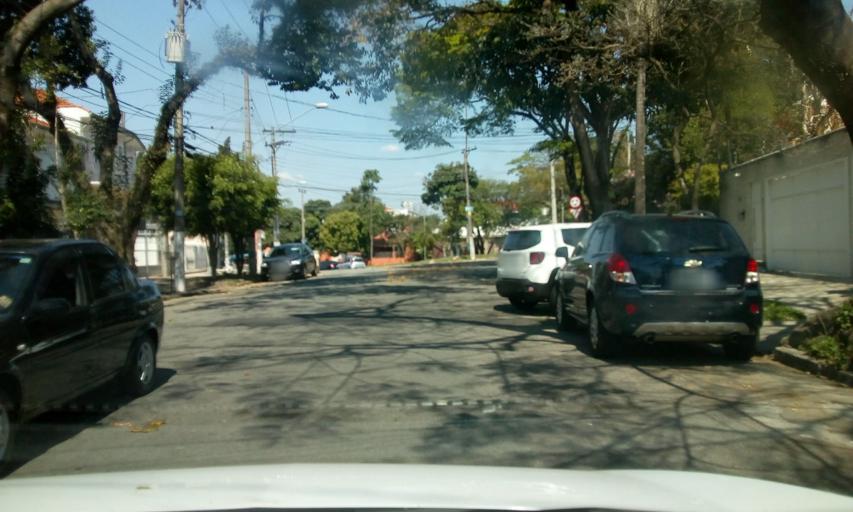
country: BR
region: Sao Paulo
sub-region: Osasco
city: Osasco
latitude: -23.5212
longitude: -46.7175
